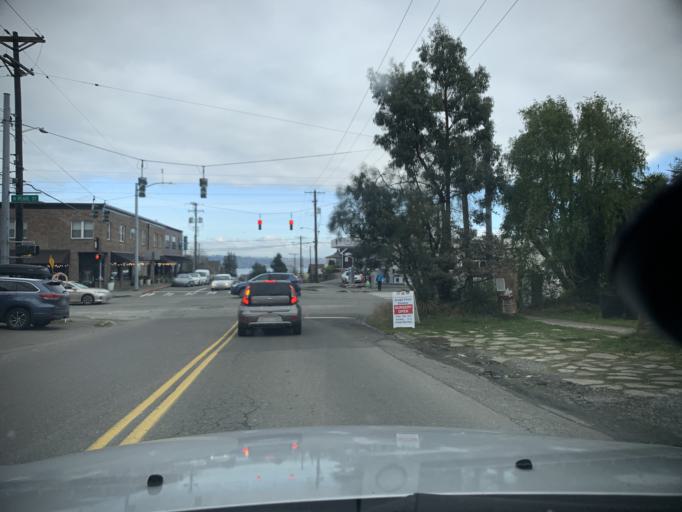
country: US
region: Washington
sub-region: Pierce County
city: Fircrest
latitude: 47.2981
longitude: -122.5159
